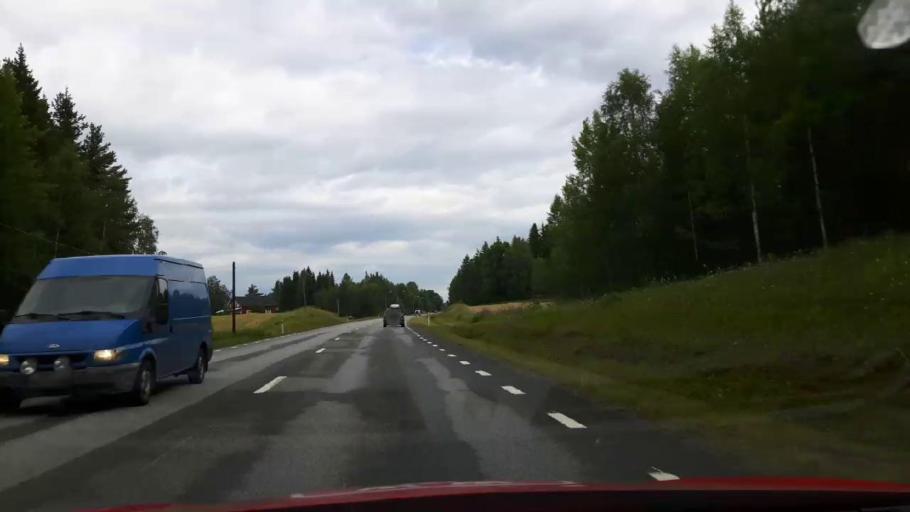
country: SE
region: Jaemtland
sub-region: Stroemsunds Kommun
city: Stroemsund
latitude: 63.6565
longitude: 15.3853
